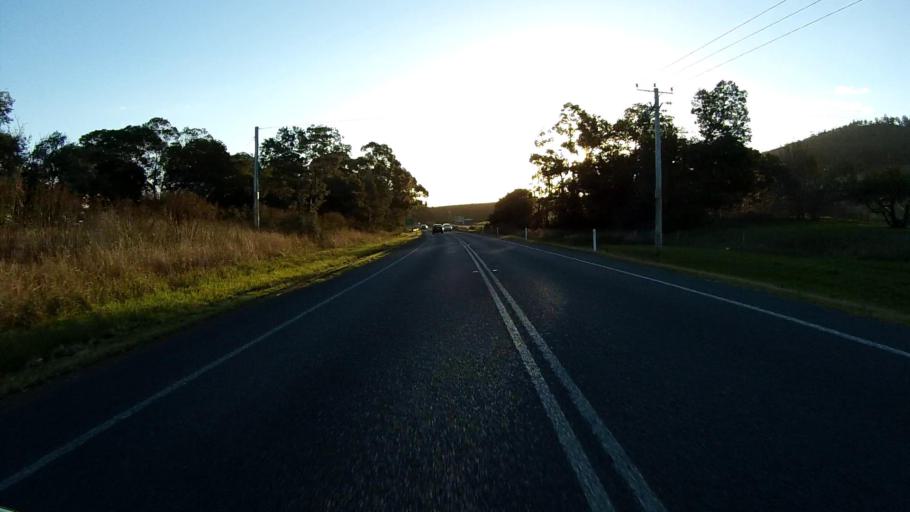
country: AU
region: Tasmania
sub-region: Sorell
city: Sorell
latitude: -42.8004
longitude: 147.6204
